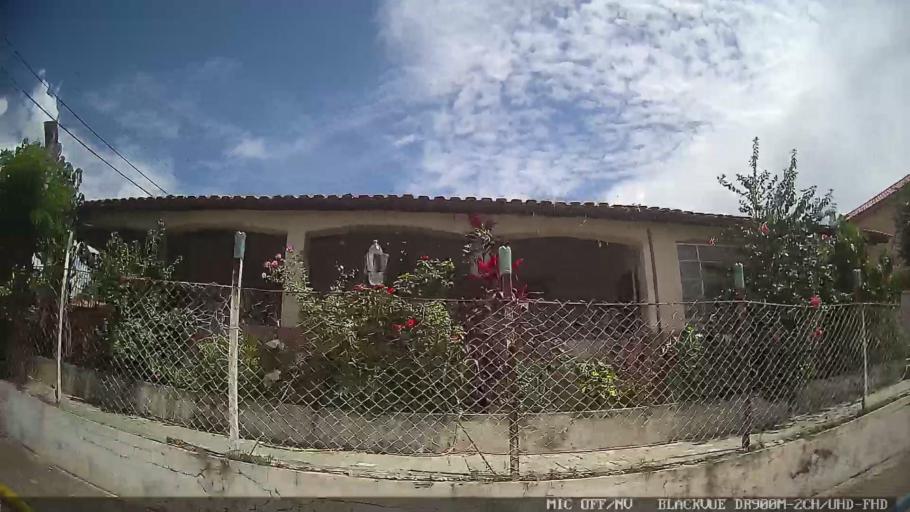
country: BR
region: Sao Paulo
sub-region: Conchas
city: Conchas
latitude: -23.0156
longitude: -48.0156
